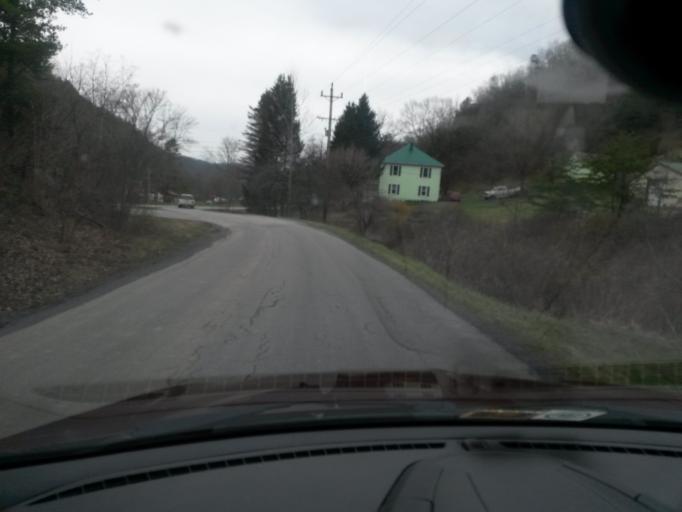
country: US
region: Virginia
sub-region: Bath County
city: Warm Springs
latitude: 38.0110
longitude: -79.8746
